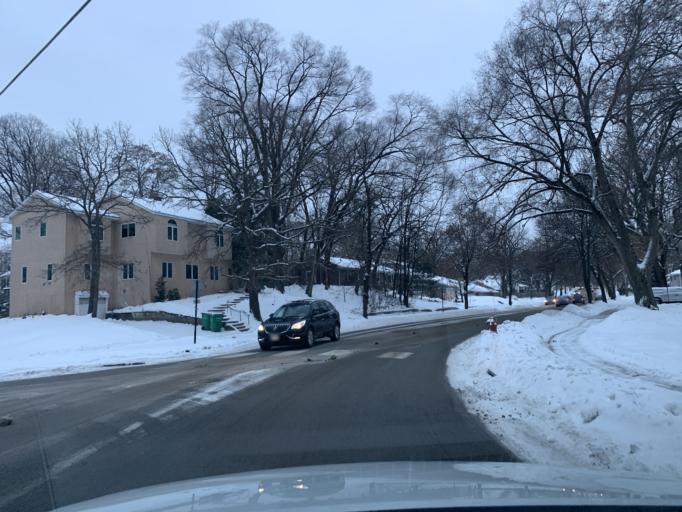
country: US
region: Minnesota
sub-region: Hennepin County
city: Saint Louis Park
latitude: 44.9253
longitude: -93.3418
